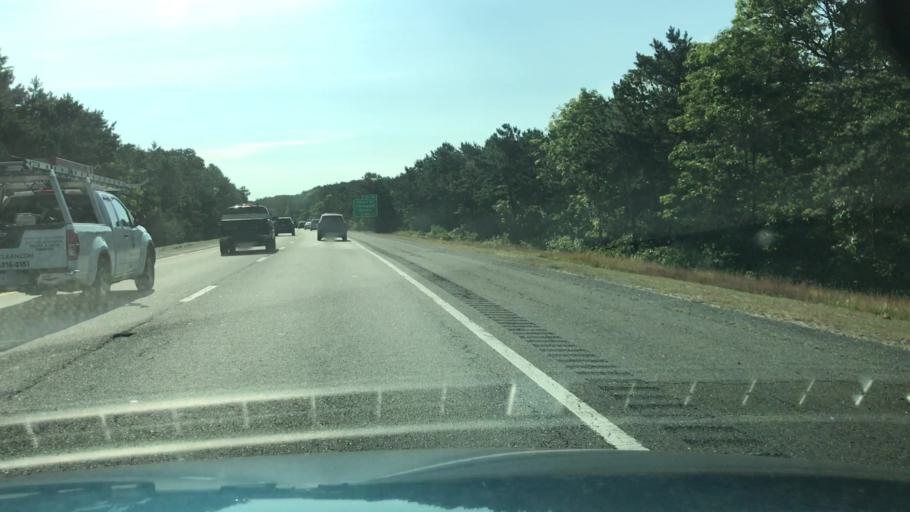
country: US
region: Massachusetts
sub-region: Barnstable County
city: Yarmouth Port
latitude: 41.6856
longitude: -70.2431
